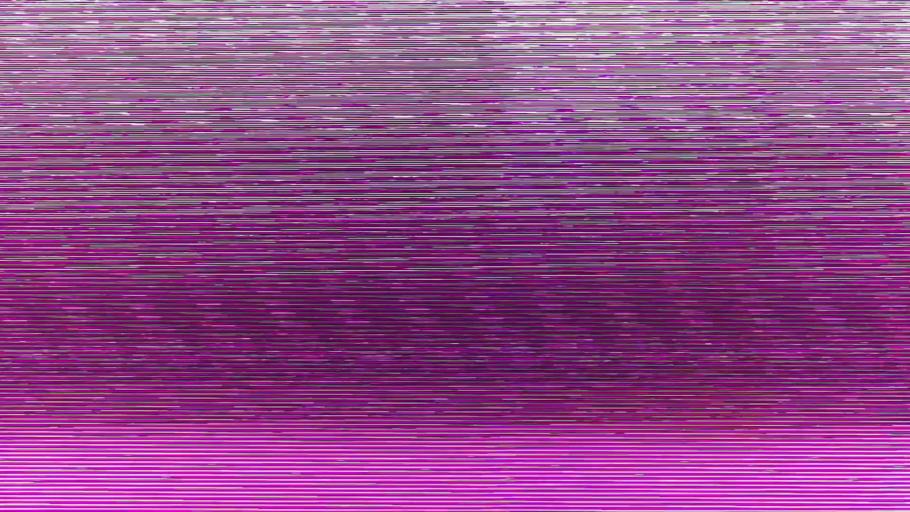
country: US
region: Michigan
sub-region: Washtenaw County
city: Ypsilanti
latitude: 42.2342
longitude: -83.6139
